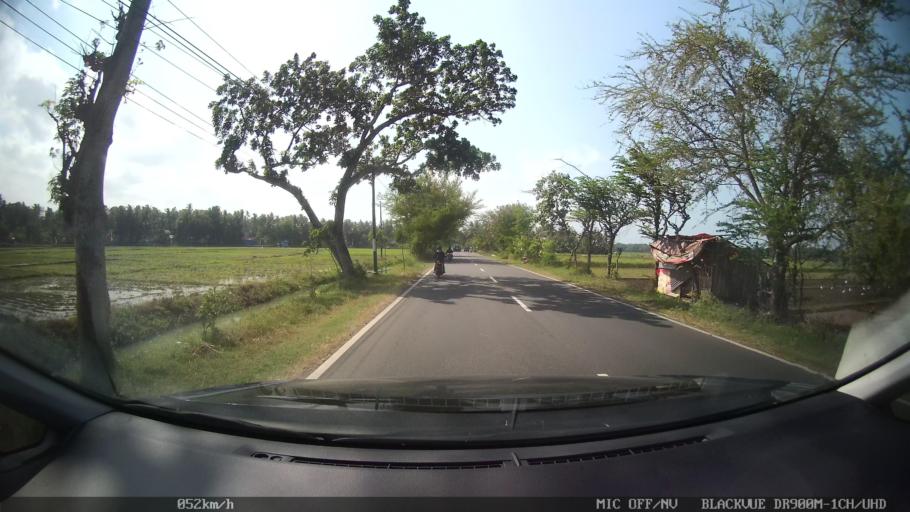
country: ID
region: Daerah Istimewa Yogyakarta
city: Srandakan
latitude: -7.9325
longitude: 110.2138
